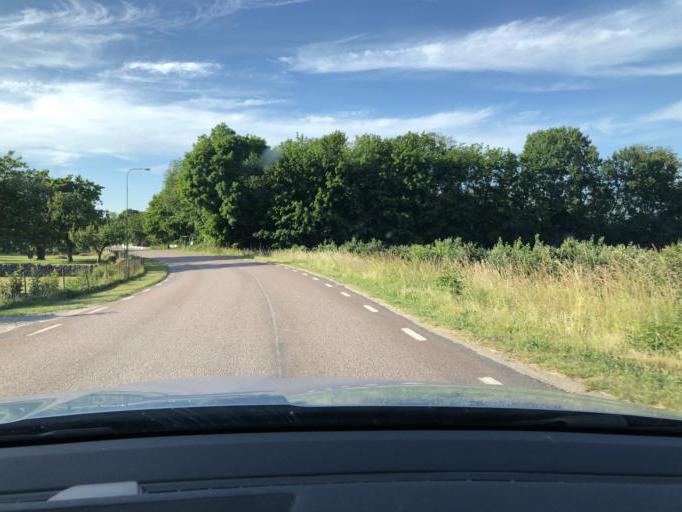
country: SE
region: Blekinge
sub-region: Solvesborgs Kommun
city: Soelvesborg
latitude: 56.1512
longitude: 14.6033
